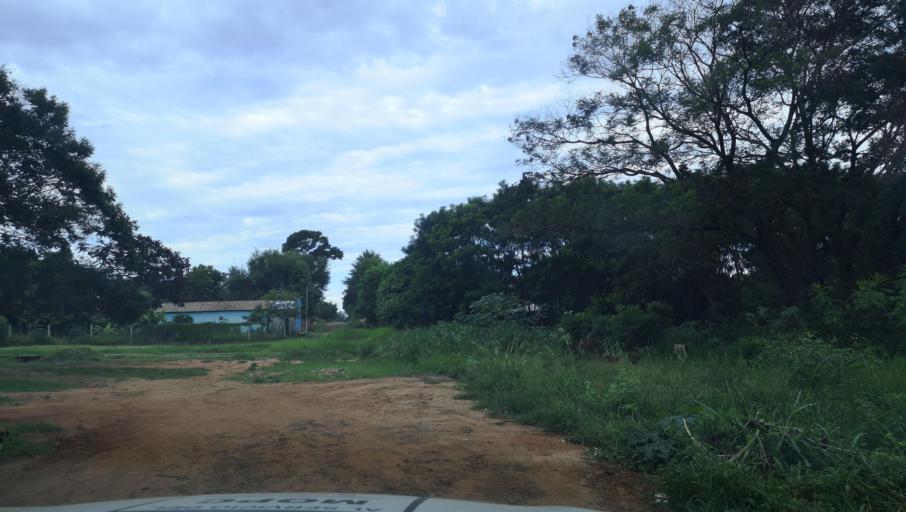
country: PY
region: San Pedro
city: Capiibary
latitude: -24.7310
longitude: -56.0216
